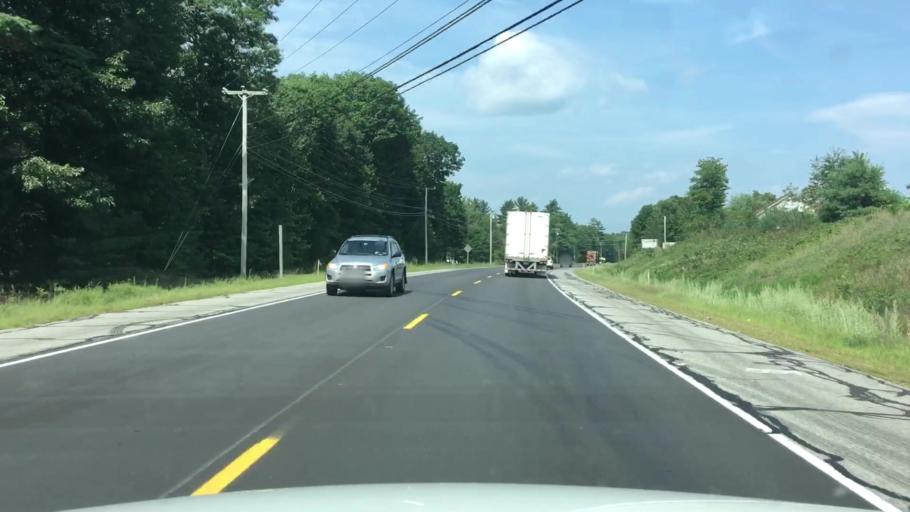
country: US
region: Maine
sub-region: Androscoggin County
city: Turner
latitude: 44.2736
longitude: -70.2700
